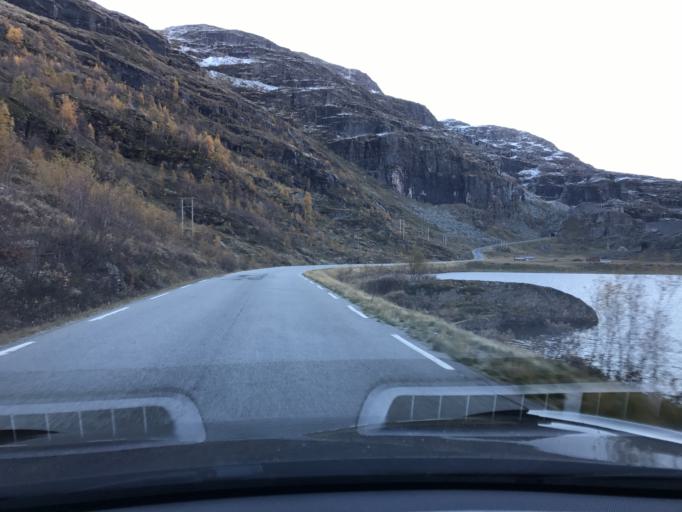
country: NO
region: Sogn og Fjordane
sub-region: Laerdal
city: Laerdalsoyri
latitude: 60.8063
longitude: 7.5612
